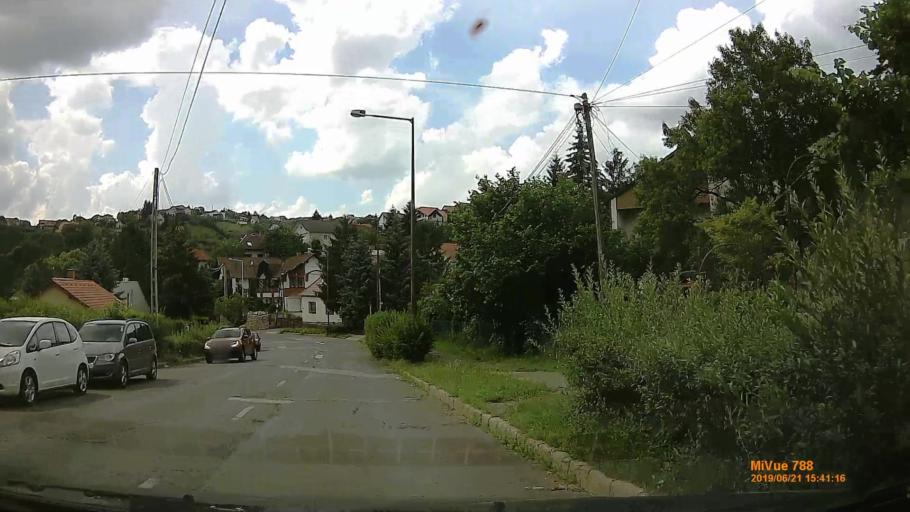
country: HU
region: Baranya
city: Pecs
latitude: 46.0845
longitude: 18.2089
